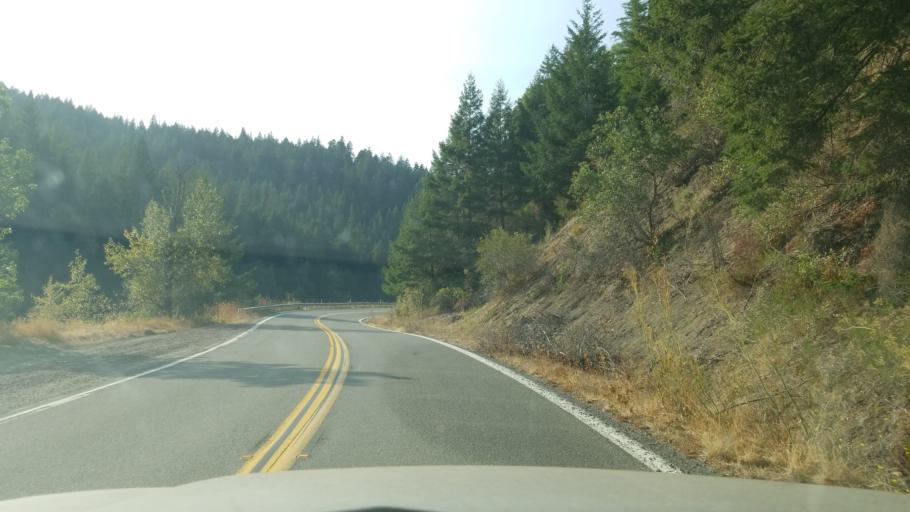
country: US
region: California
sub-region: Humboldt County
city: Redway
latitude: 40.2664
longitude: -123.8467
